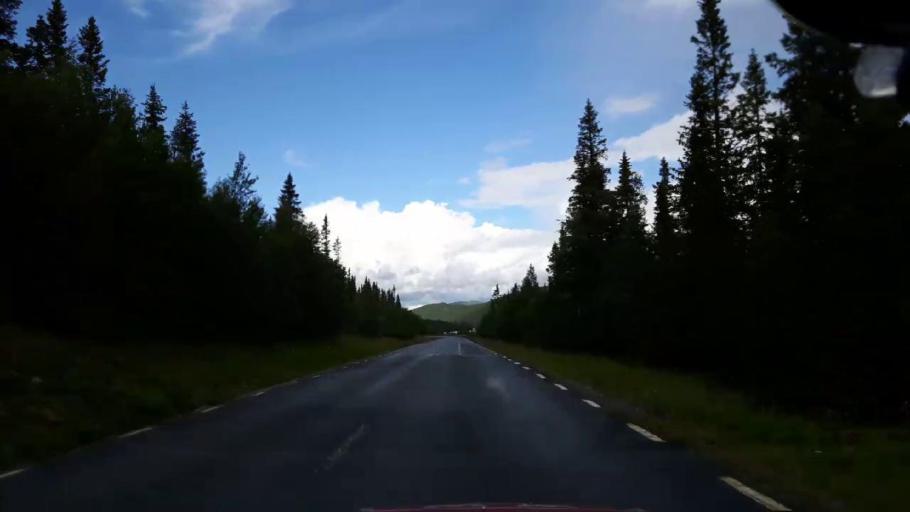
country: SE
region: Vaesterbotten
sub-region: Vilhelmina Kommun
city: Sjoberg
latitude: 65.0051
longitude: 15.1899
